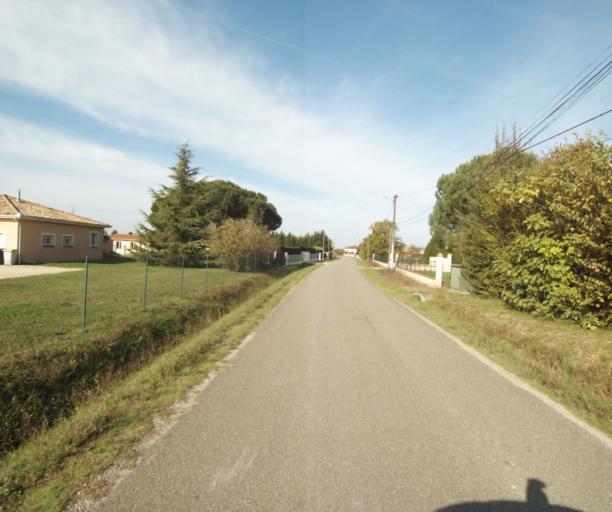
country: FR
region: Midi-Pyrenees
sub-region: Departement du Tarn-et-Garonne
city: Nohic
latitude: 43.9111
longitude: 1.4443
